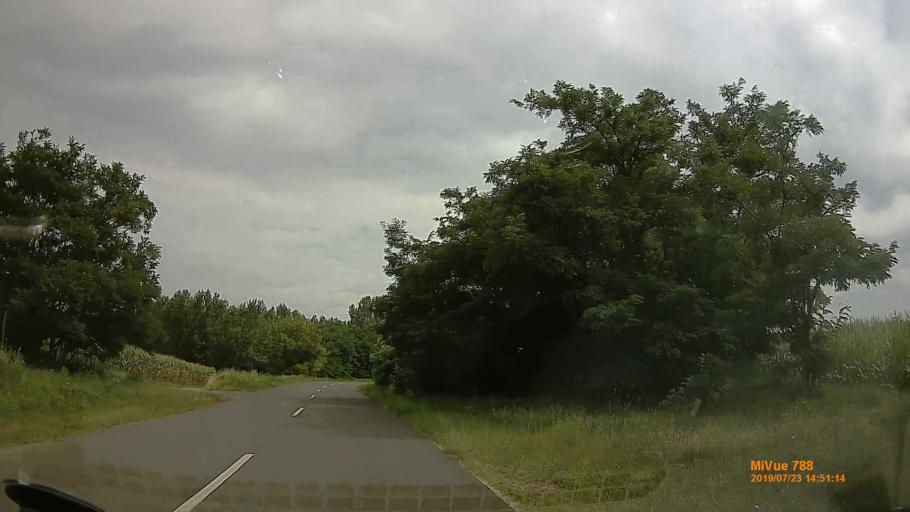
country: HU
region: Szabolcs-Szatmar-Bereg
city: Kalmanhaza
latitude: 47.8843
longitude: 21.6512
